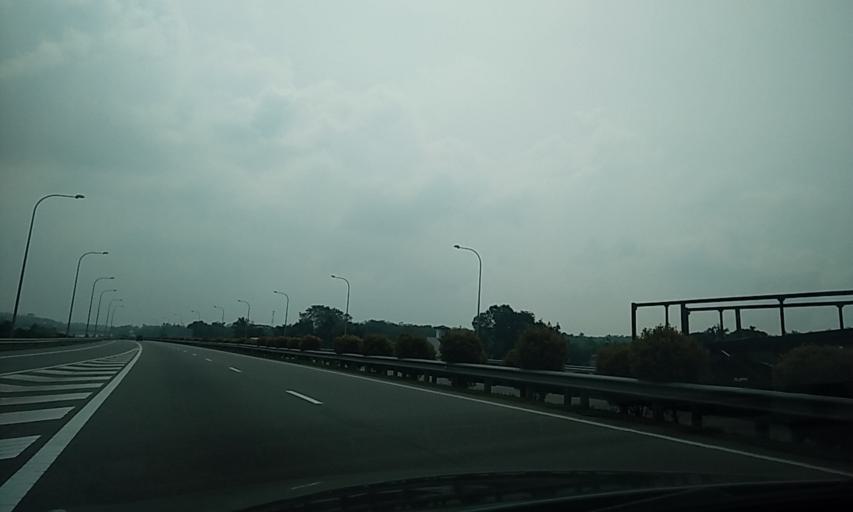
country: LK
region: Western
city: Homagama
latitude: 6.8822
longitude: 79.9767
